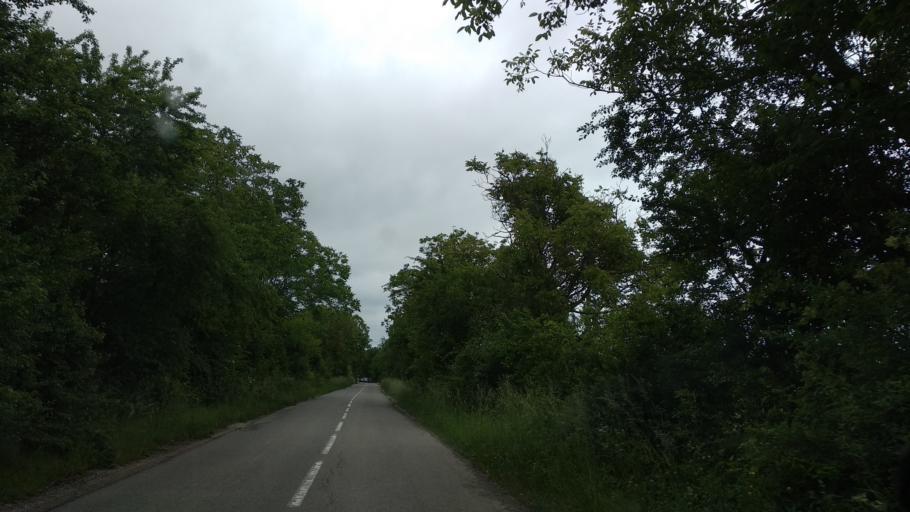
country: SK
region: Nitriansky
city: Trencianske Teplice
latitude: 48.7920
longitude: 18.1330
